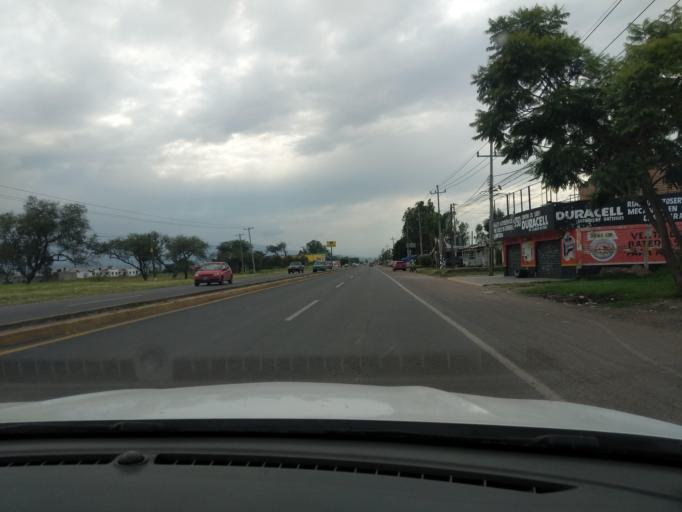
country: MX
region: Jalisco
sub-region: El Salto
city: Galaxia Bonito Jalisco
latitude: 20.5090
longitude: -103.2015
